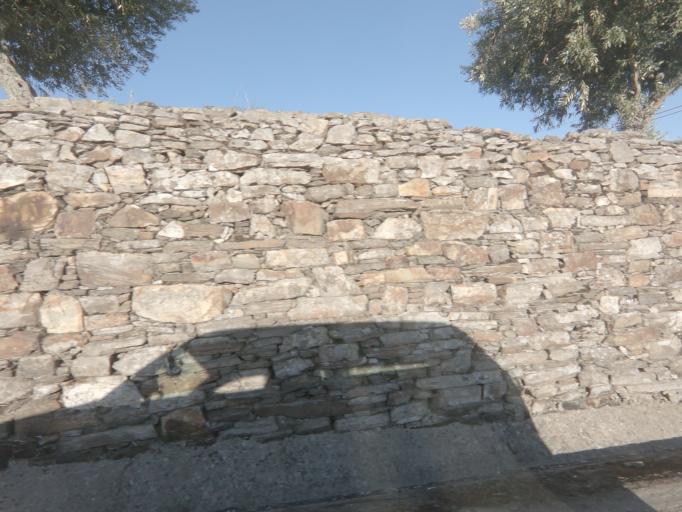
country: PT
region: Vila Real
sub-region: Peso da Regua
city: Godim
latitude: 41.1614
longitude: -7.8176
